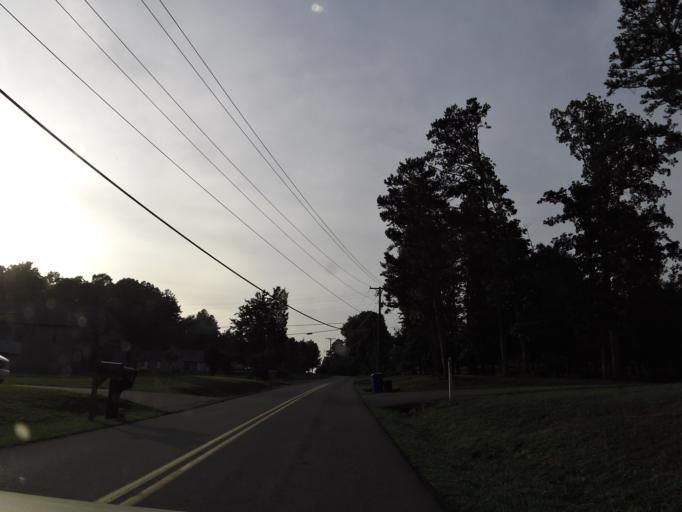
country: US
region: Tennessee
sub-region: Sevier County
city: Seymour
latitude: 35.8648
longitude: -83.7907
